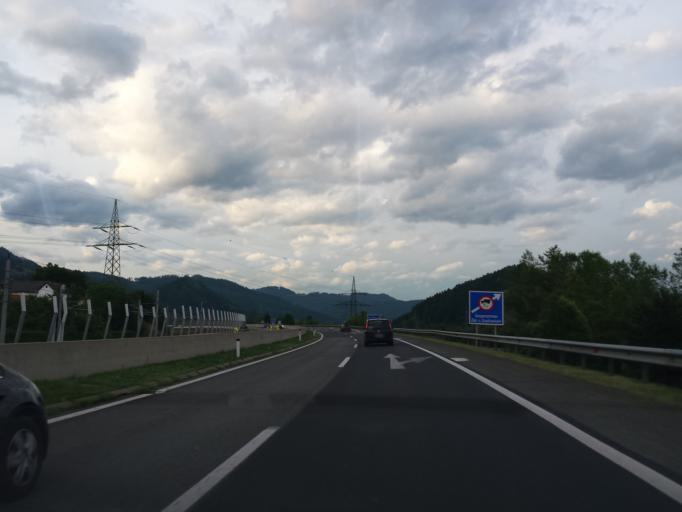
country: AT
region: Styria
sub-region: Politischer Bezirk Leoben
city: Sankt Stefan ob Leoben
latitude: 47.3220
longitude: 14.9695
